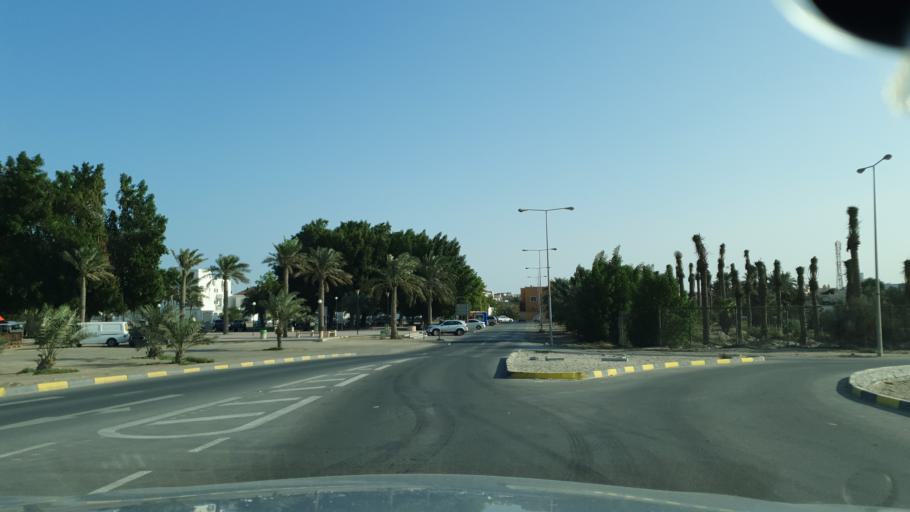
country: BH
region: Manama
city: Jidd Hafs
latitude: 26.2245
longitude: 50.4593
